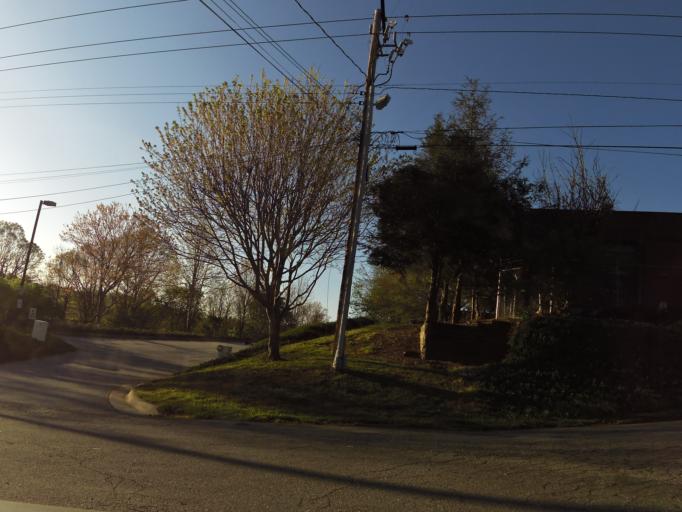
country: US
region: North Carolina
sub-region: Buncombe County
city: Asheville
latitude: 35.5875
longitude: -82.5788
